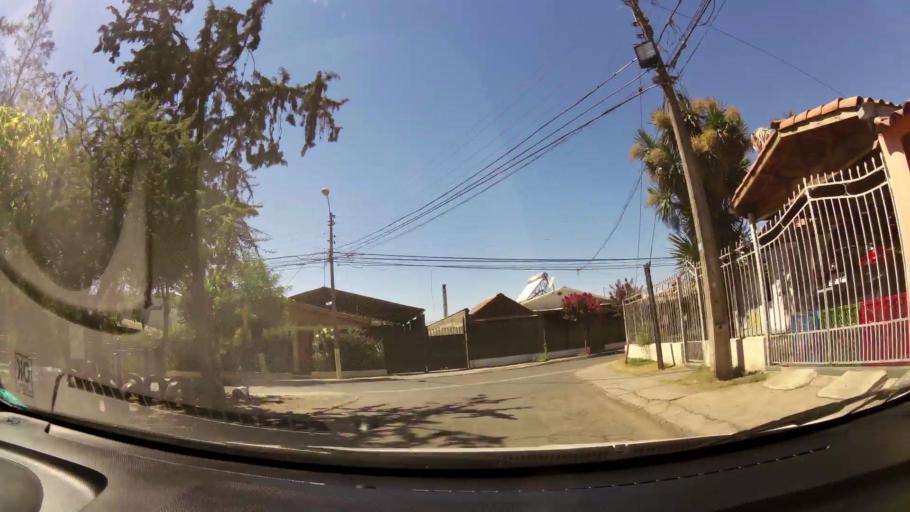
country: CL
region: O'Higgins
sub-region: Provincia de Cachapoal
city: Rancagua
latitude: -34.1612
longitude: -70.7548
